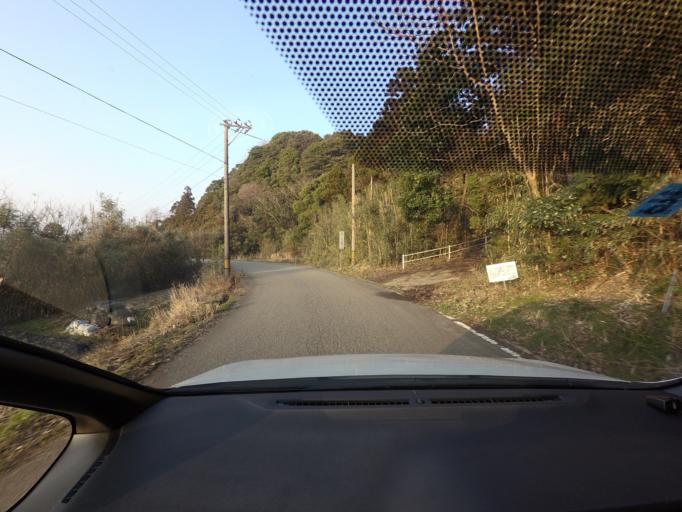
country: JP
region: Ishikawa
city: Nanao
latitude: 37.1640
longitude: 137.0325
